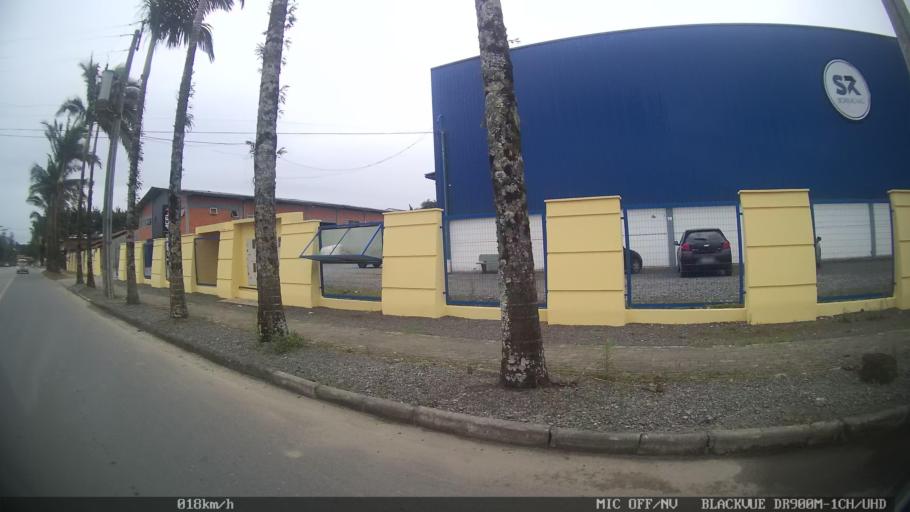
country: BR
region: Santa Catarina
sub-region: Joinville
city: Joinville
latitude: -26.1980
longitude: -48.9097
